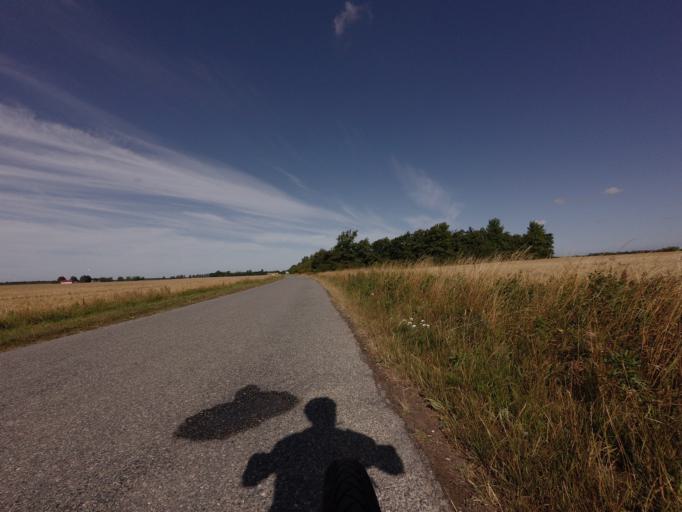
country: DK
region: North Denmark
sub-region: Hjorring Kommune
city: Vra
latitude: 57.3911
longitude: 9.9747
